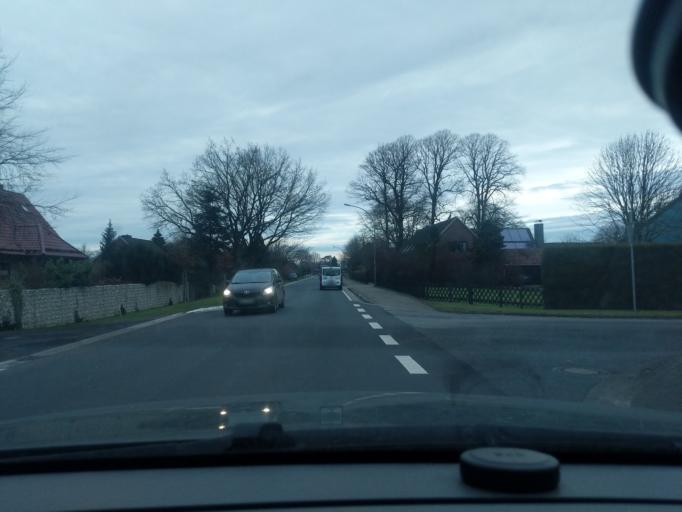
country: DE
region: Lower Saxony
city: Sauensiek
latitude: 53.3823
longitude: 9.5974
